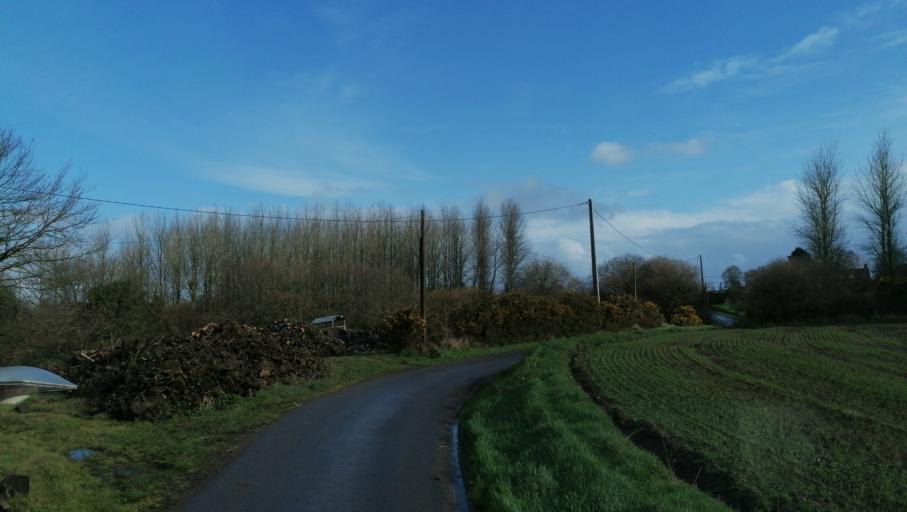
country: FR
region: Brittany
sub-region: Departement des Cotes-d'Armor
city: Lanrodec
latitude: 48.4934
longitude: -3.0138
